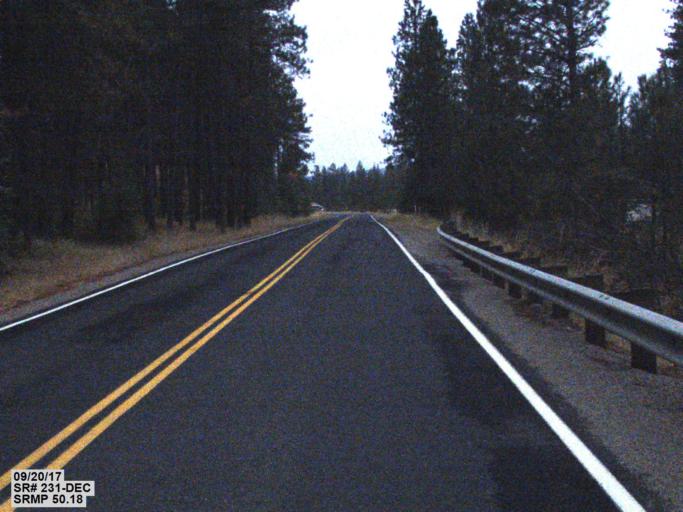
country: US
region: Washington
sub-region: Spokane County
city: Fairchild Air Force Base
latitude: 47.9067
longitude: -117.8105
